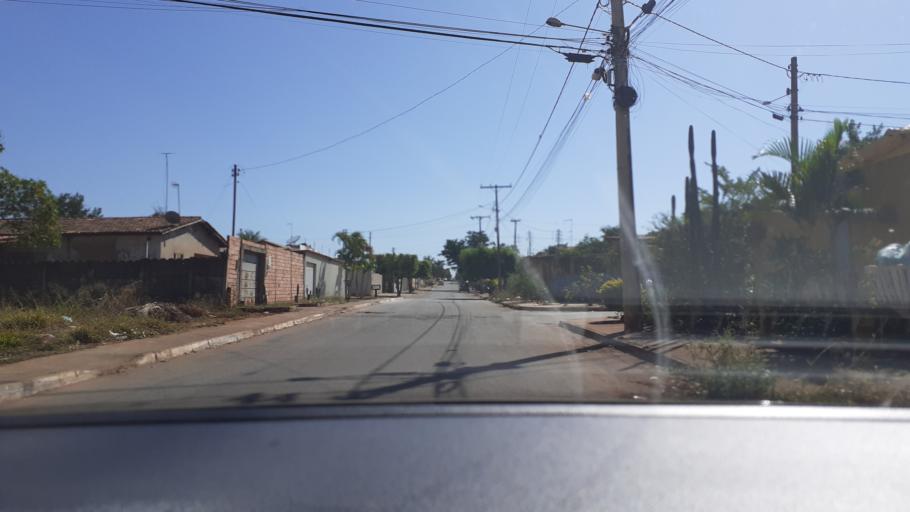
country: BR
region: Goias
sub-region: Aparecida De Goiania
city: Aparecida de Goiania
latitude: -16.8410
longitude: -49.2481
